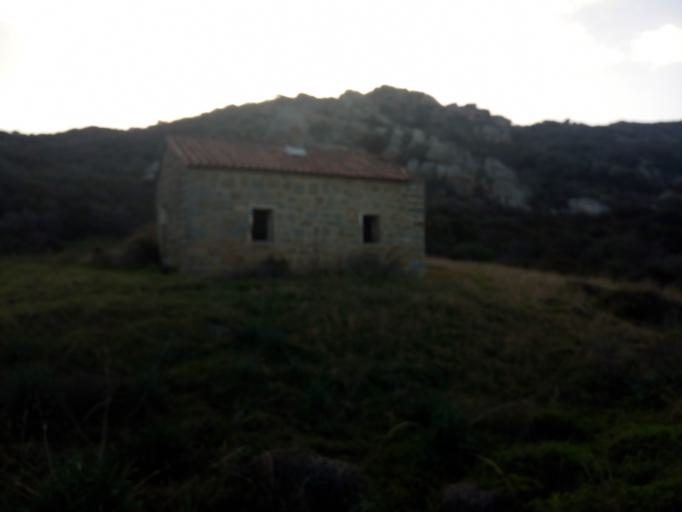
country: FR
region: Corsica
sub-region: Departement de la Corse-du-Sud
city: Appietto
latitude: 42.0693
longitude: 8.7222
